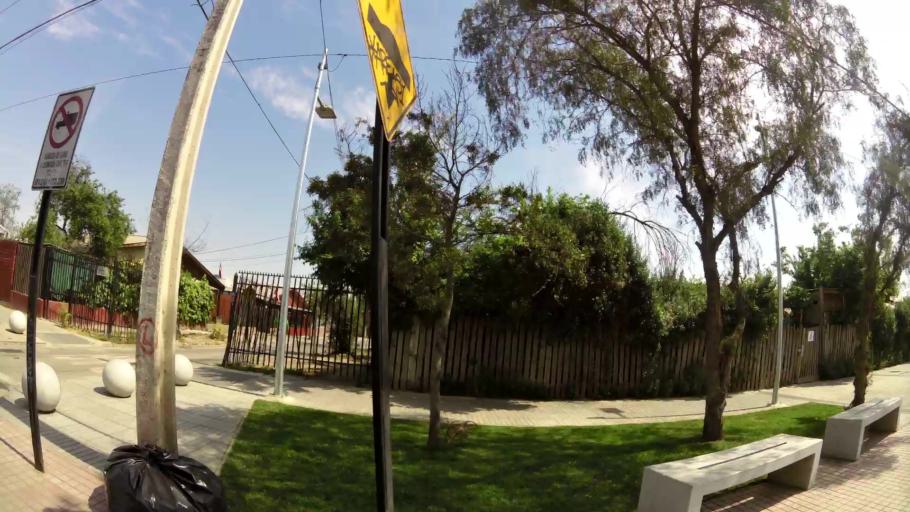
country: CL
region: Santiago Metropolitan
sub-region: Provincia de Santiago
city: La Pintana
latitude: -33.5549
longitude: -70.6518
